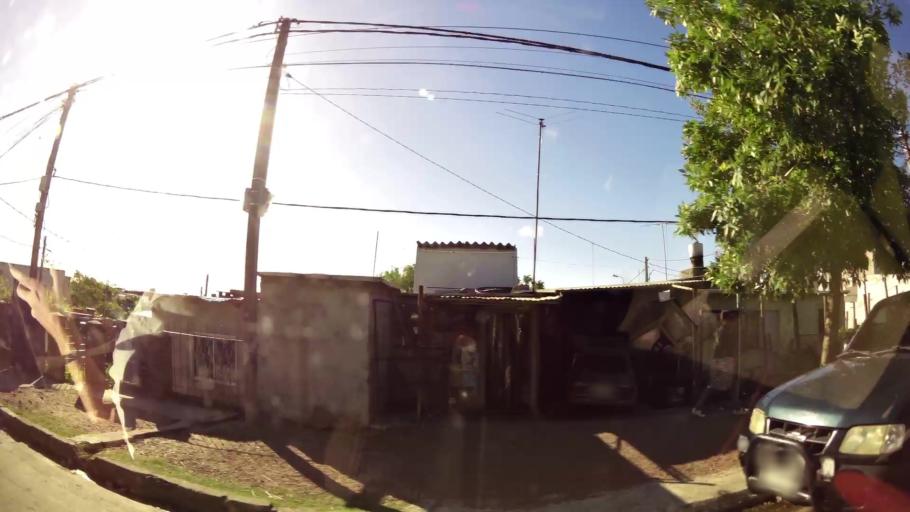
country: UY
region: Montevideo
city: Montevideo
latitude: -34.8465
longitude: -56.2466
